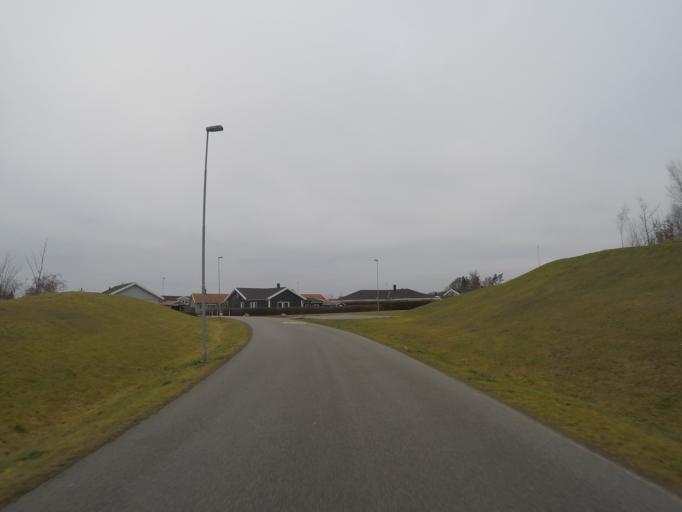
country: SE
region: Skane
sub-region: Eslovs Kommun
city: Eslov
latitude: 55.7568
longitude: 13.3724
